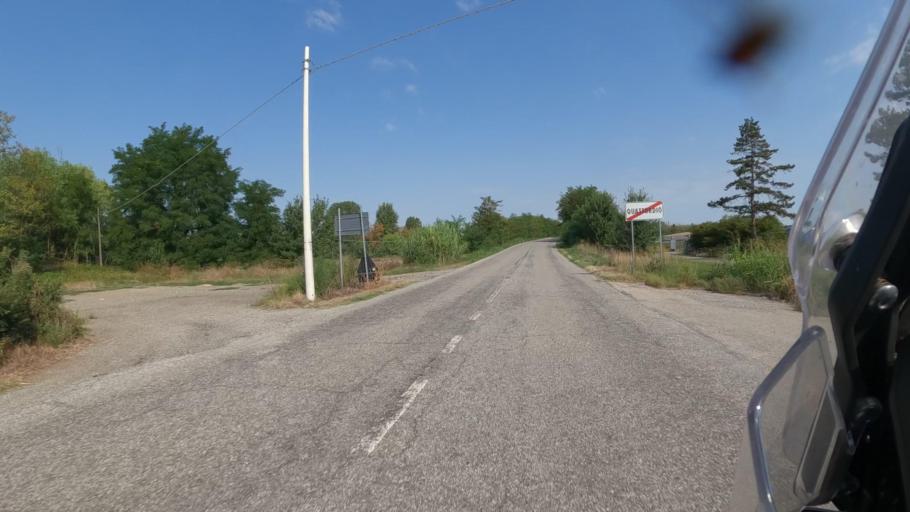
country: IT
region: Piedmont
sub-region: Provincia di Alessandria
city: Quattordio
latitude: 44.9056
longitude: 8.4016
